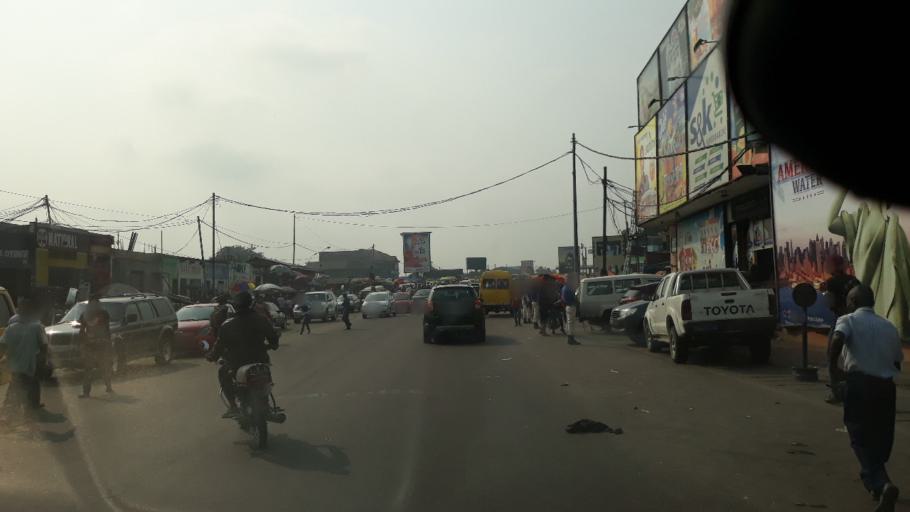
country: CD
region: Kinshasa
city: Kinshasa
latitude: -4.4080
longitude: 15.2566
